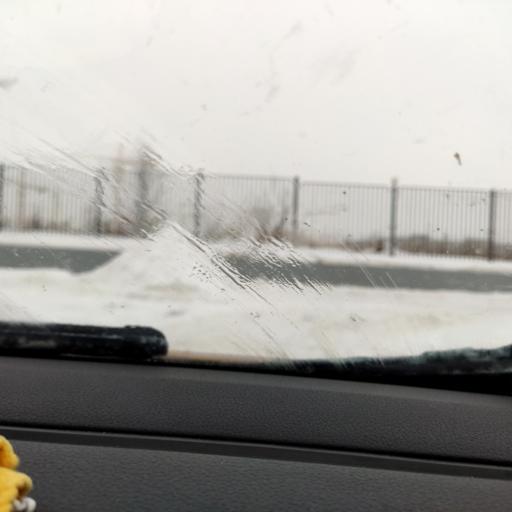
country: RU
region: Moskovskaya
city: Skolkovo
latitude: 55.6822
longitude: 37.3333
